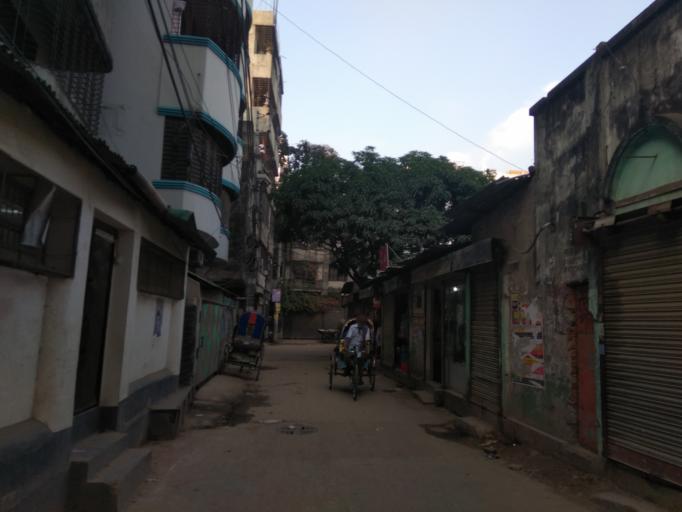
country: BD
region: Dhaka
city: Azimpur
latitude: 23.8104
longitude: 90.3784
